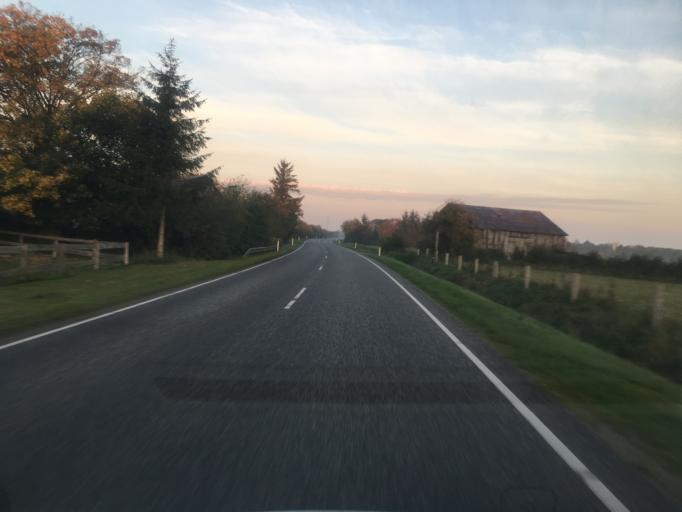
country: DK
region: South Denmark
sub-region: Tonder Kommune
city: Logumkloster
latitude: 55.0336
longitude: 9.0444
